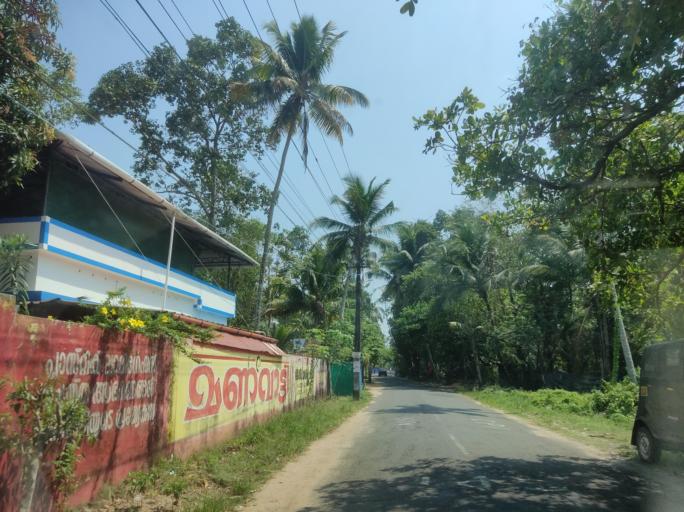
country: IN
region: Kerala
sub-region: Alappuzha
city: Vayalar
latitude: 9.6945
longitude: 76.3029
